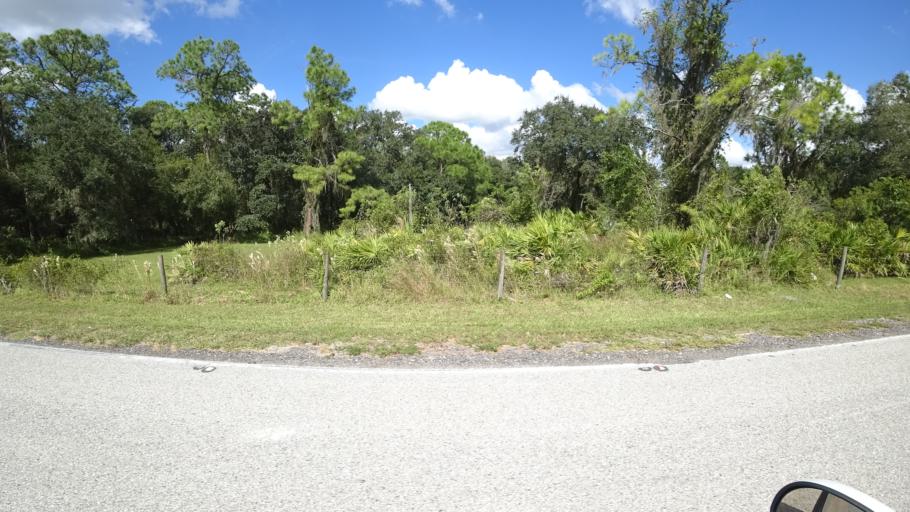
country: US
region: Florida
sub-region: Sarasota County
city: Lake Sarasota
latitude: 27.3392
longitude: -82.1622
